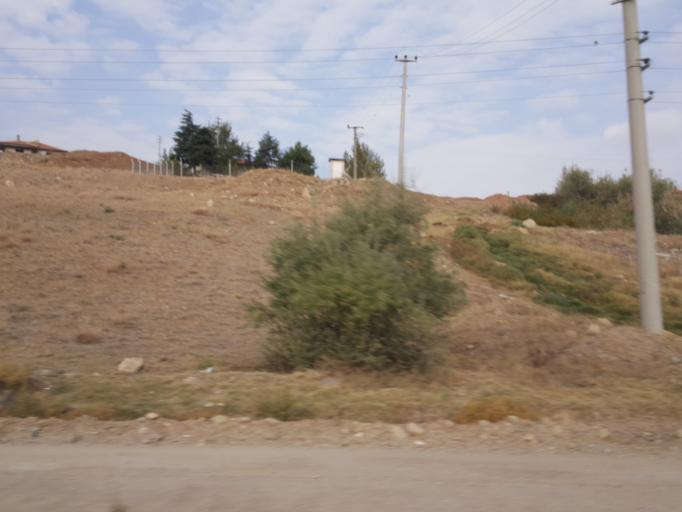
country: TR
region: Kirikkale
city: Bahsili
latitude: 39.8050
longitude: 33.4663
